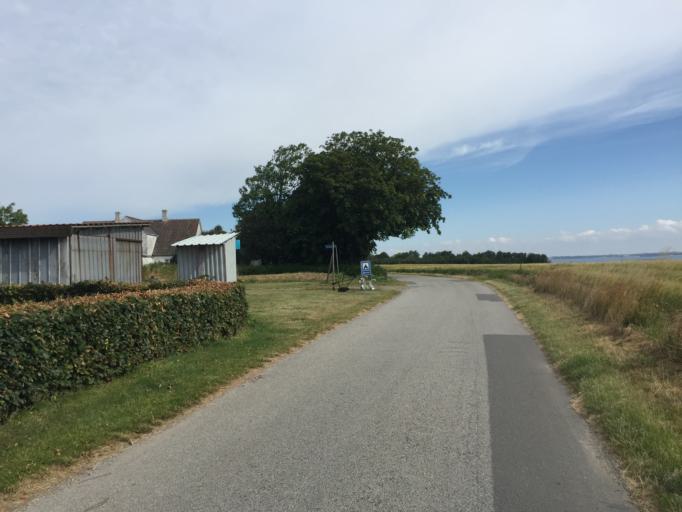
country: DK
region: Zealand
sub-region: Slagelse Kommune
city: Skaelskor
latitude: 55.2175
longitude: 11.1864
